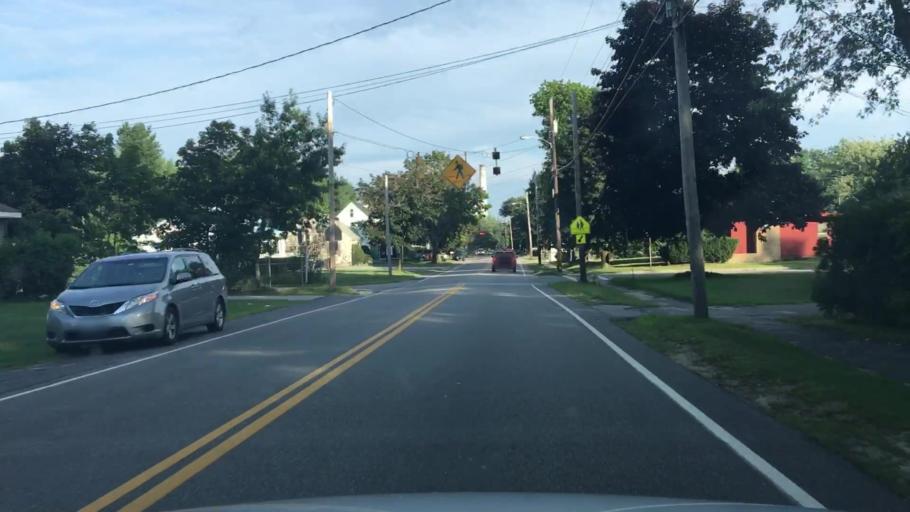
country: US
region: Maine
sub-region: Cumberland County
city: Westbrook
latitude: 43.6896
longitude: -70.3630
